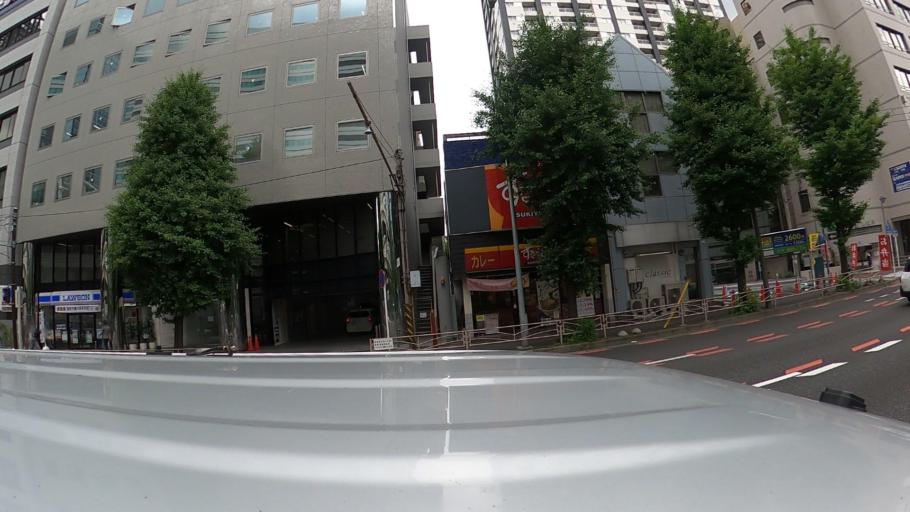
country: JP
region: Kanagawa
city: Yokohama
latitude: 35.4690
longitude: 139.6266
